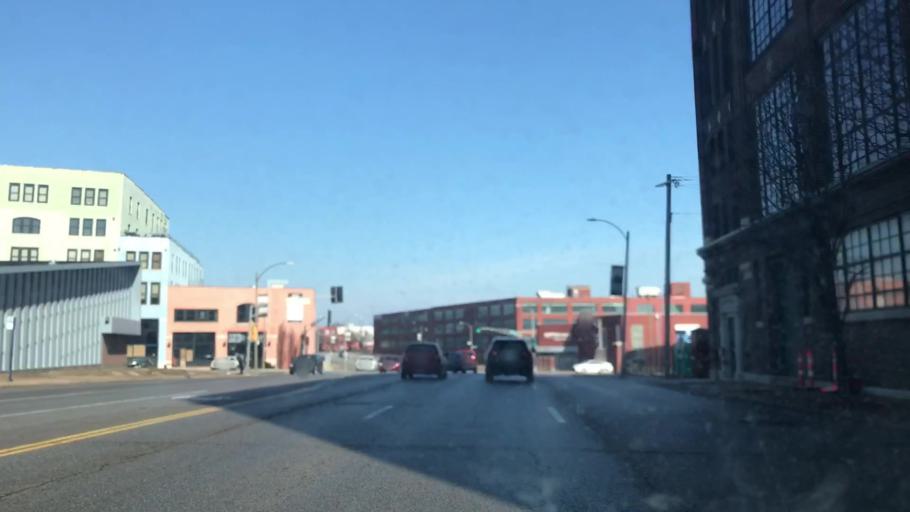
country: US
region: Missouri
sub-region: City of Saint Louis
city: St. Louis
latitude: 38.6344
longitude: -90.2136
